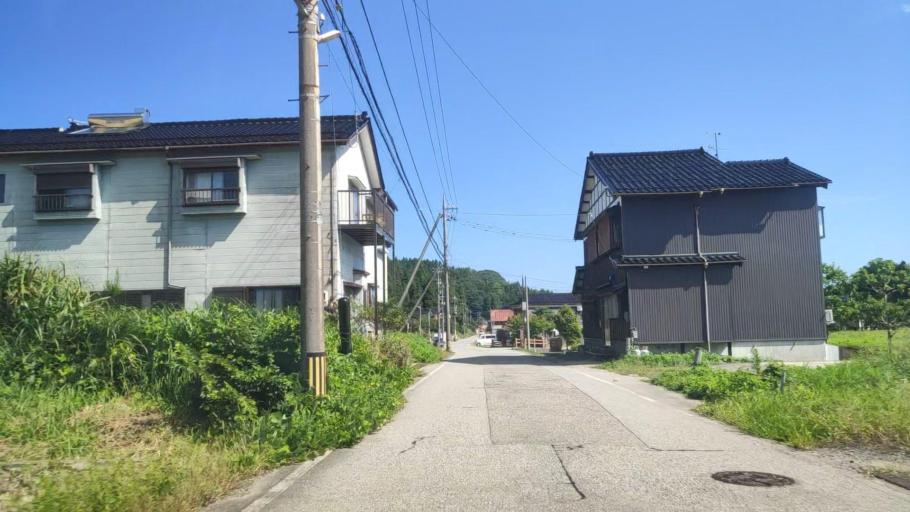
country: JP
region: Ishikawa
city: Nanao
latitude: 37.3794
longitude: 136.8802
